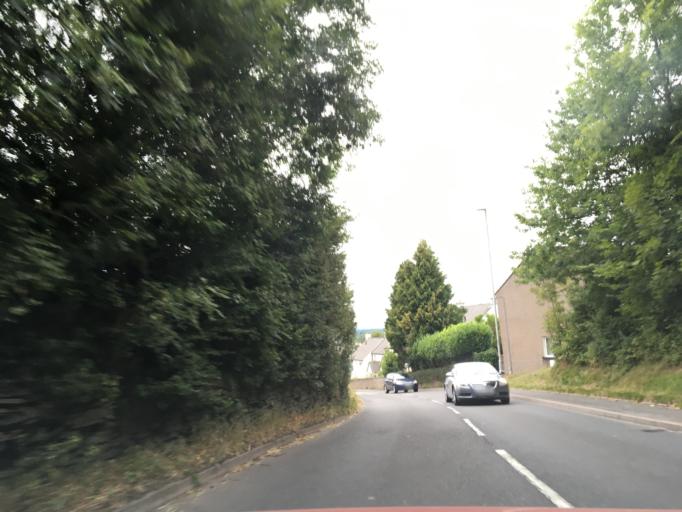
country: GB
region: Wales
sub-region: Blaenau Gwent
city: Brynmawr
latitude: 51.8915
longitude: -3.2404
